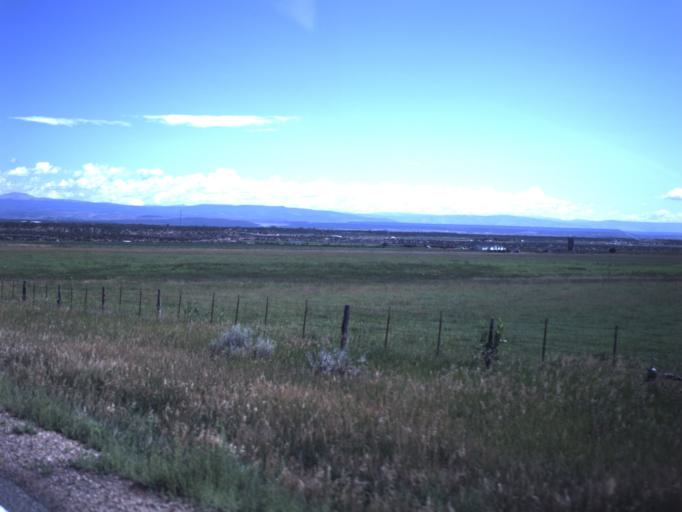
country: US
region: Utah
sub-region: Duchesne County
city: Duchesne
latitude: 40.3365
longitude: -110.4079
